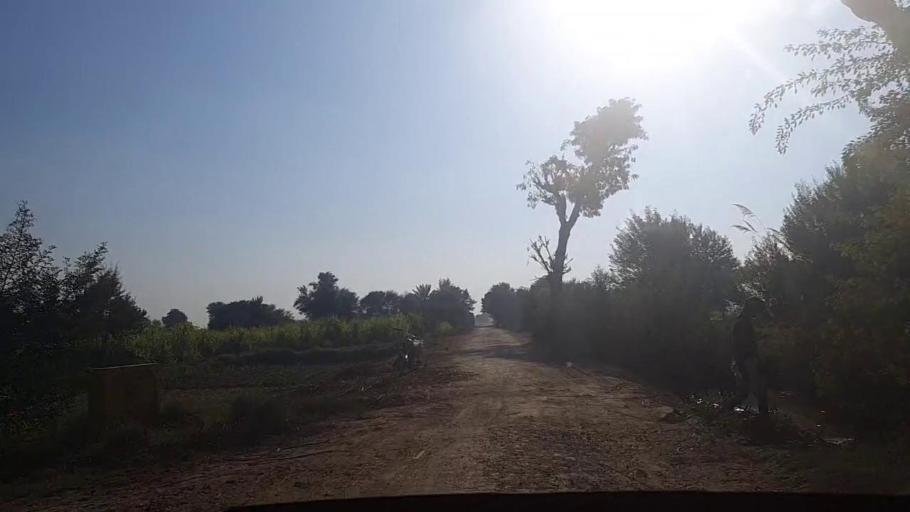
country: PK
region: Sindh
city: Gambat
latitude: 27.3670
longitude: 68.4613
